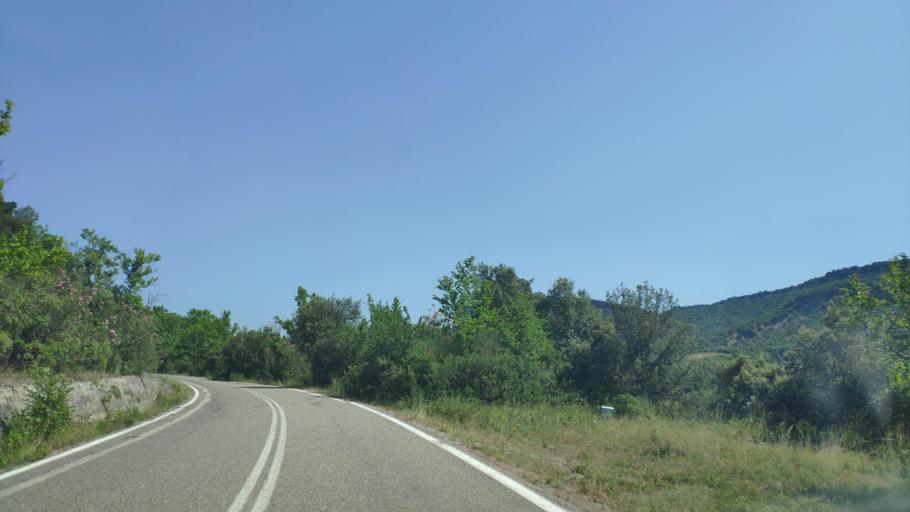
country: GR
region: West Greece
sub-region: Nomos Aitolias kai Akarnanias
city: Lepenou
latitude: 38.7742
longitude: 21.3358
